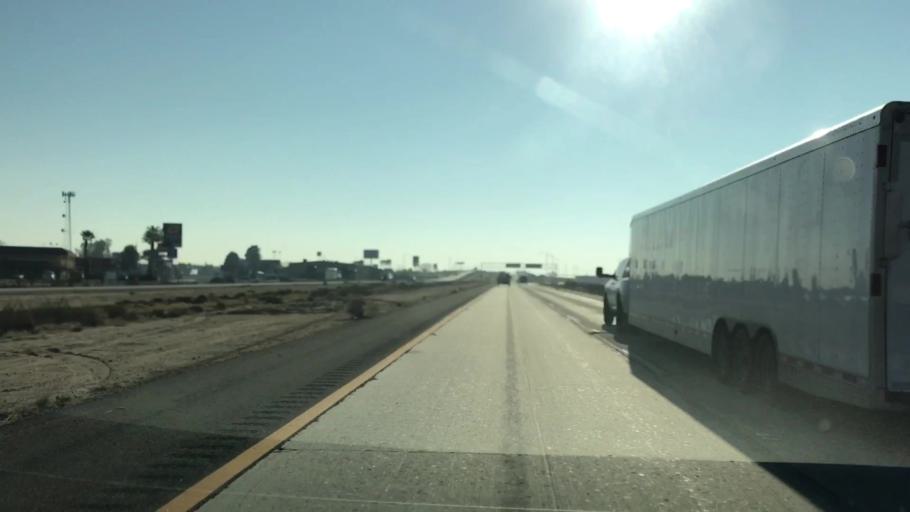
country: US
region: California
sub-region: Kern County
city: Buttonwillow
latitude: 35.4041
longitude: -119.4050
